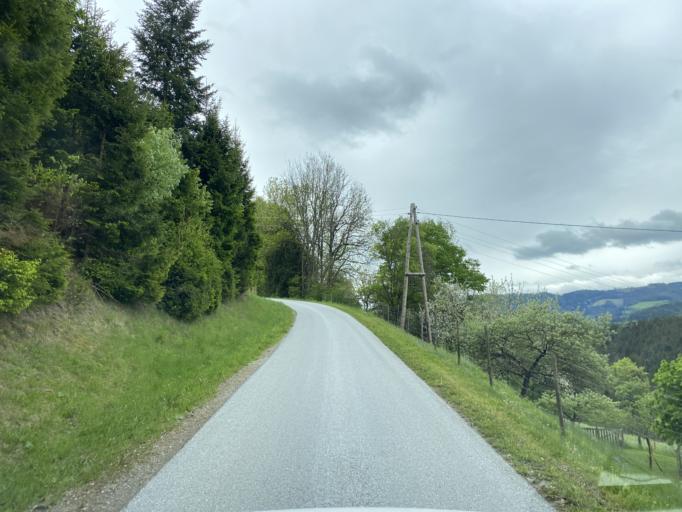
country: AT
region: Styria
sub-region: Politischer Bezirk Weiz
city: Koglhof
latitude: 47.3311
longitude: 15.6999
